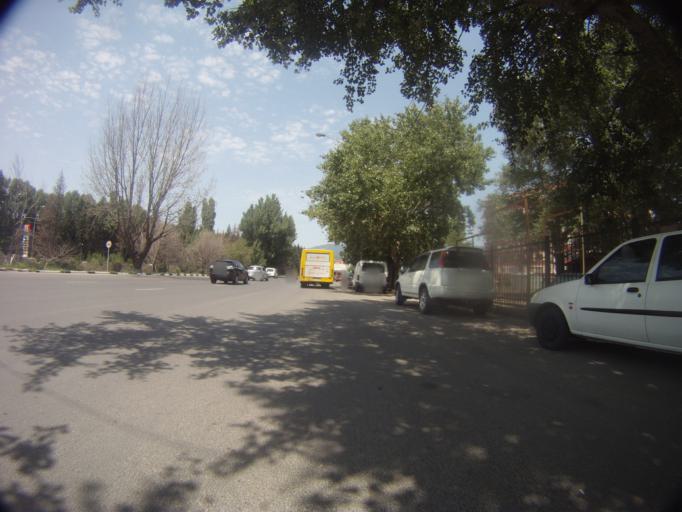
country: GE
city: Zahesi
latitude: 41.7978
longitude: 44.7710
